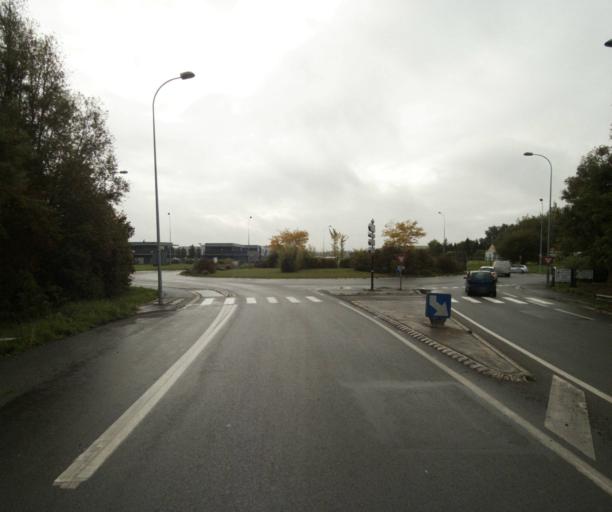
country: FR
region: Nord-Pas-de-Calais
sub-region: Departement du Nord
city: Hallennes-lez-Haubourdin
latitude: 50.6084
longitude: 2.9554
